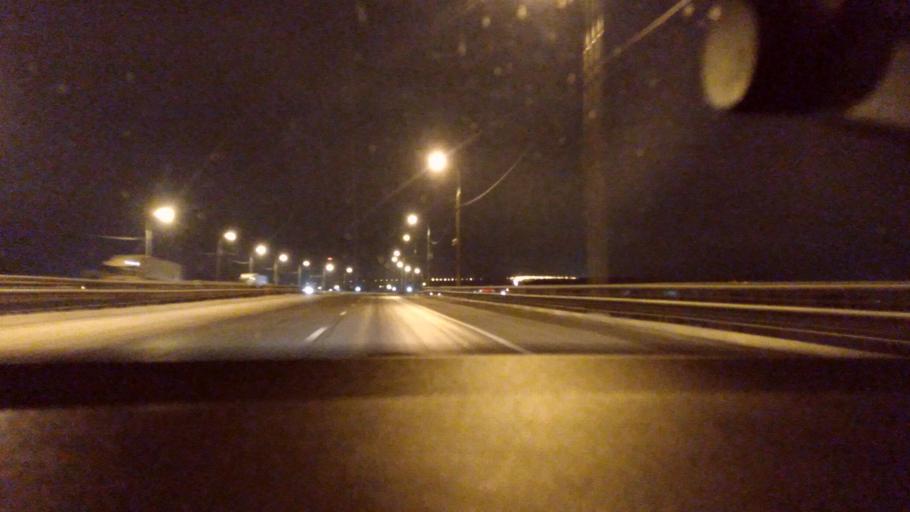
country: RU
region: Moskovskaya
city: Raduzhnyy
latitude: 55.1419
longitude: 38.7443
